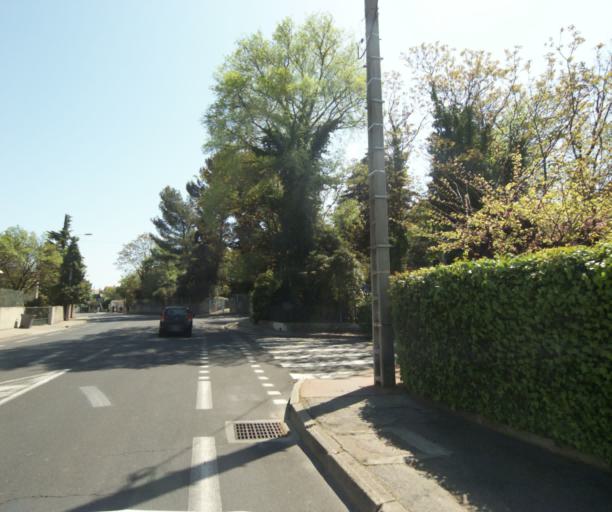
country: FR
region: Languedoc-Roussillon
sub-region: Departement de l'Herault
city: Montpellier
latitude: 43.6257
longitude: 3.8498
